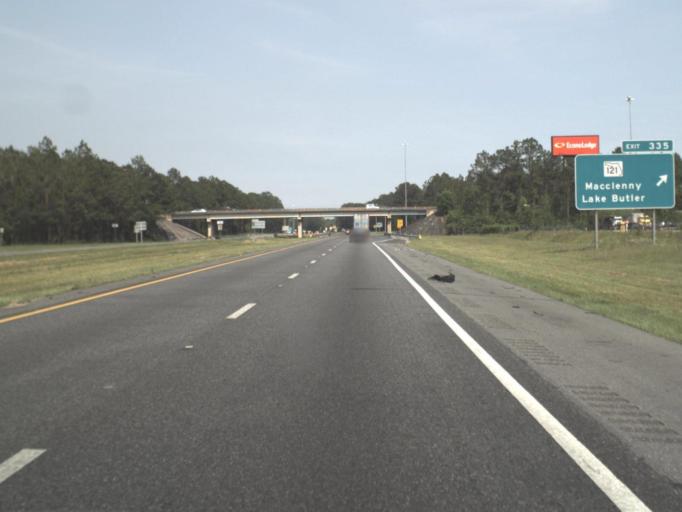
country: US
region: Florida
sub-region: Baker County
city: Macclenny
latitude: 30.2589
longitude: -82.1256
